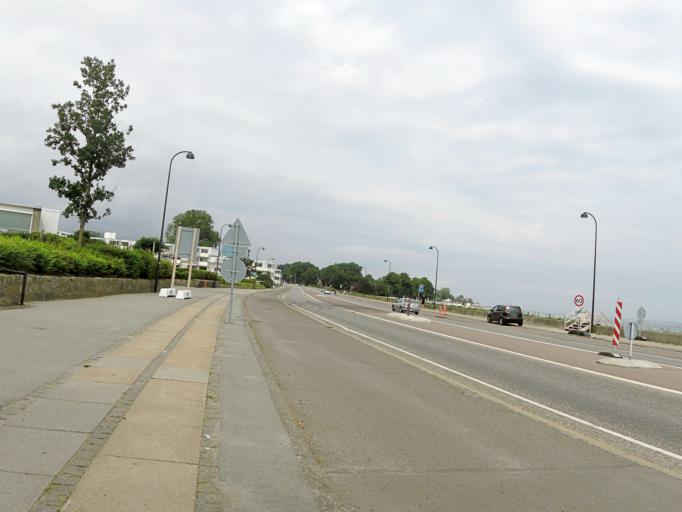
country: DK
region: Capital Region
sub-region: Gentofte Kommune
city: Charlottenlund
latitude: 55.7747
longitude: 12.5916
